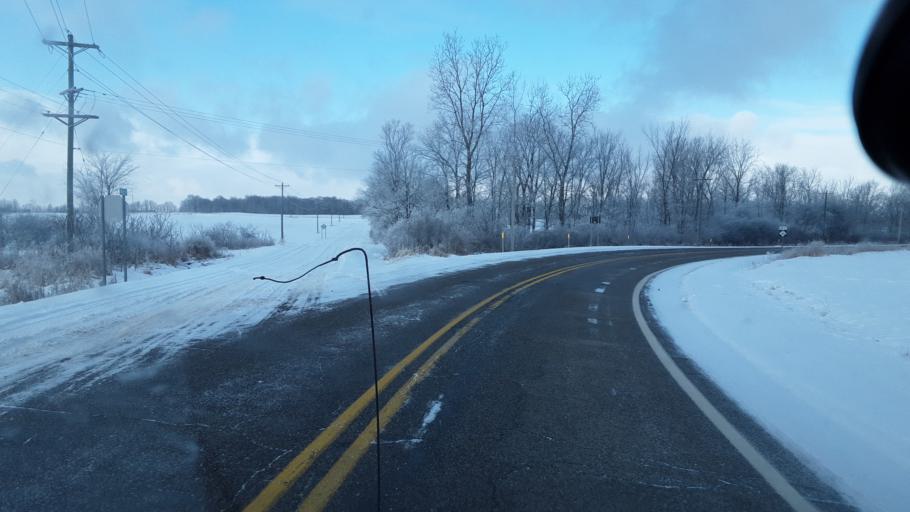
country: US
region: Michigan
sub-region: Eaton County
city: Eaton Rapids
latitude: 42.4875
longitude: -84.6200
